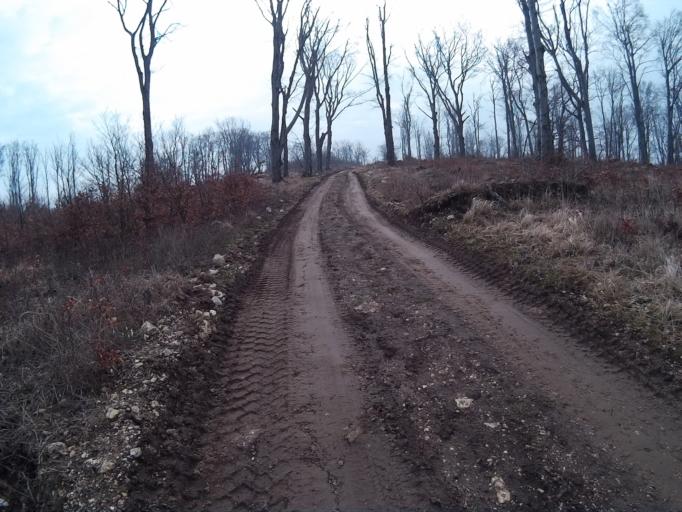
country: HU
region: Veszprem
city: Zirc
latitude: 47.1888
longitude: 17.8310
